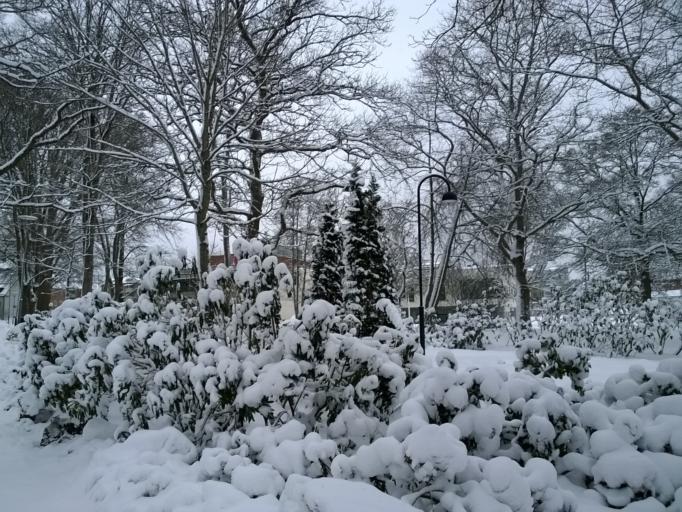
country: SE
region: Joenkoeping
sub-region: Nassjo Kommun
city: Nassjo
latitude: 57.6536
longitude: 14.7006
